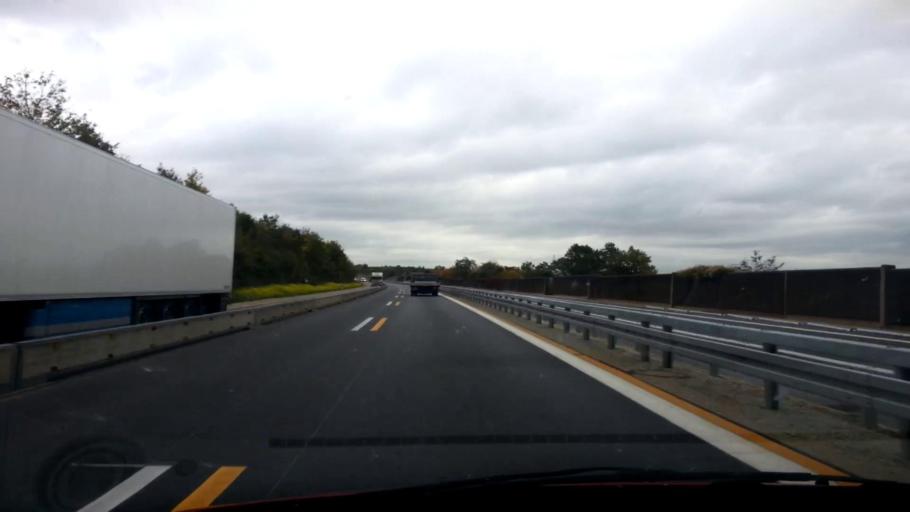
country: DE
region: Bavaria
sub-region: Upper Franconia
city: Memmelsdorf
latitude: 49.9394
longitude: 10.9591
